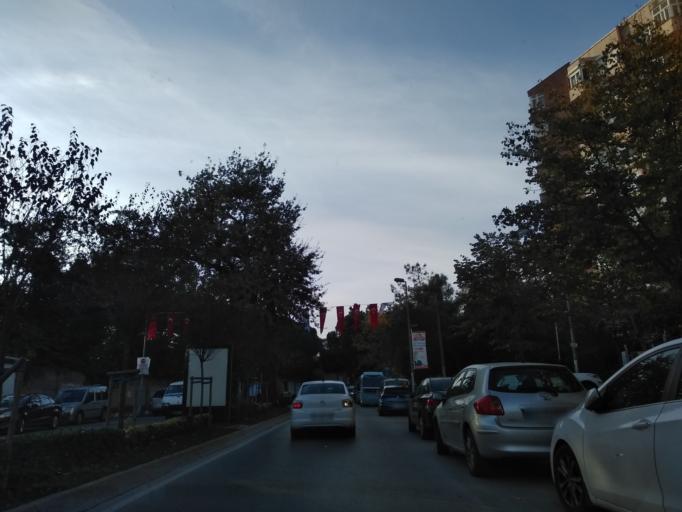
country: TR
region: Istanbul
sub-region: Atasehir
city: Atasehir
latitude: 40.9755
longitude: 29.0911
